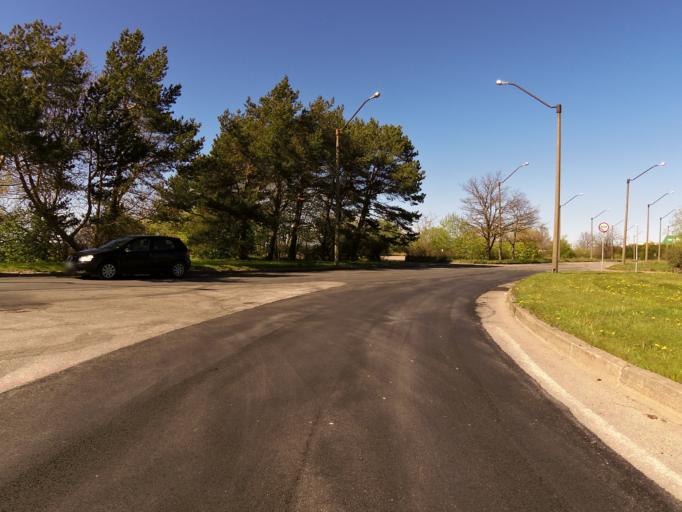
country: EE
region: Harju
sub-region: Viimsi vald
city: Viimsi
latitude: 59.4614
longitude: 24.8180
